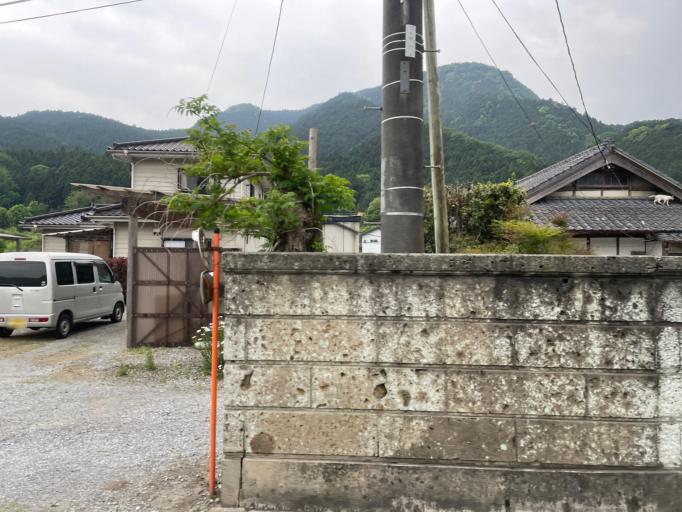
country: JP
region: Tochigi
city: Tanuma
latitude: 36.4495
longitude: 139.6416
